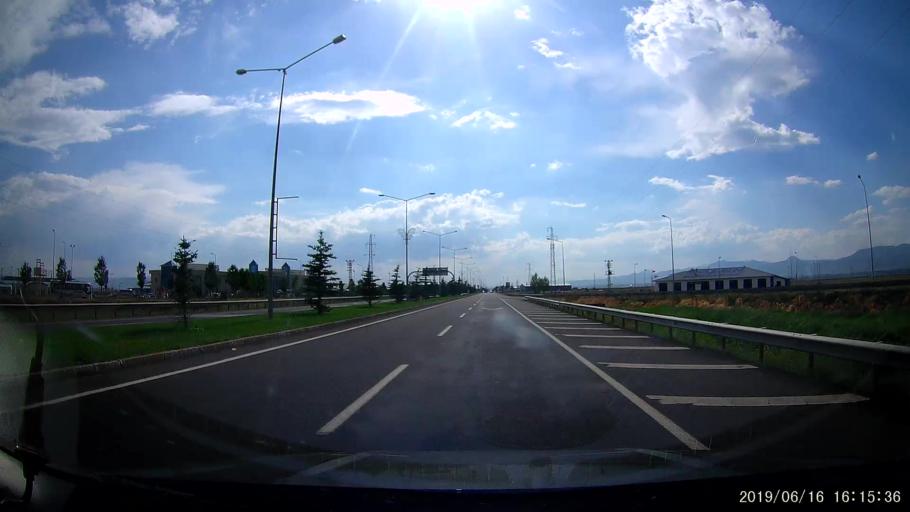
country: TR
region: Erzurum
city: Erzurum
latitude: 39.9621
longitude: 41.2227
